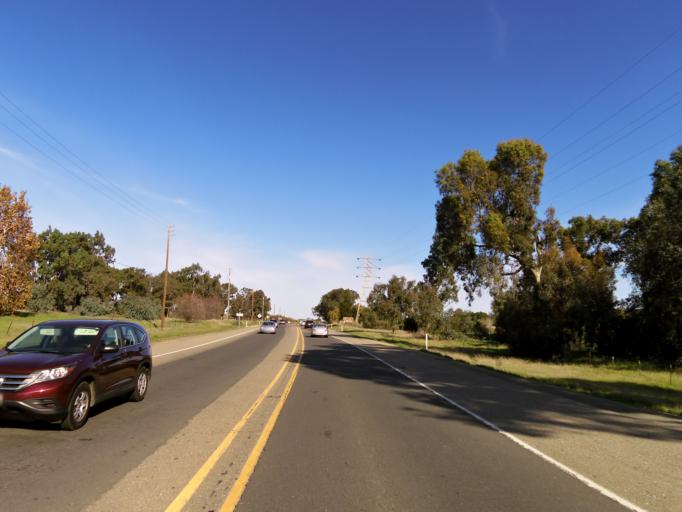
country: US
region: California
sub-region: Solano County
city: Rio Vista
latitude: 38.1082
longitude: -121.6995
